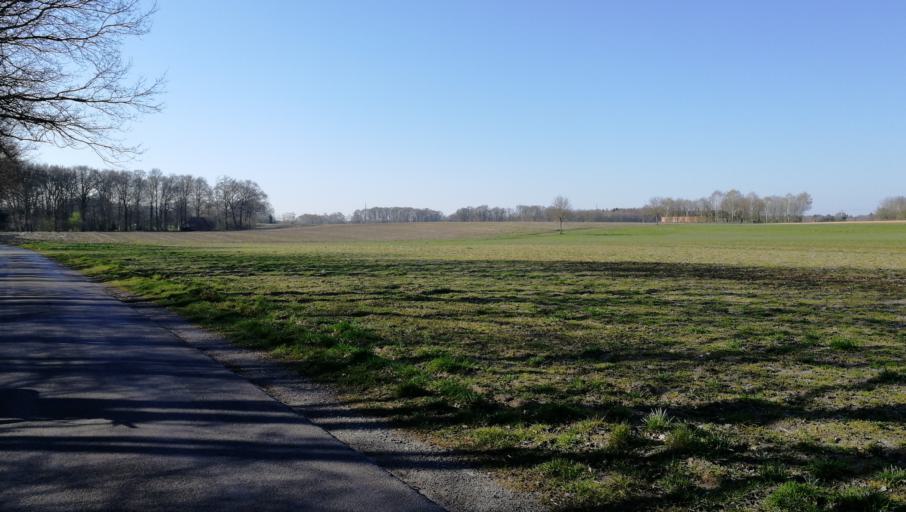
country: DE
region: Lower Saxony
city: Emsburen
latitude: 52.3997
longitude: 7.3223
